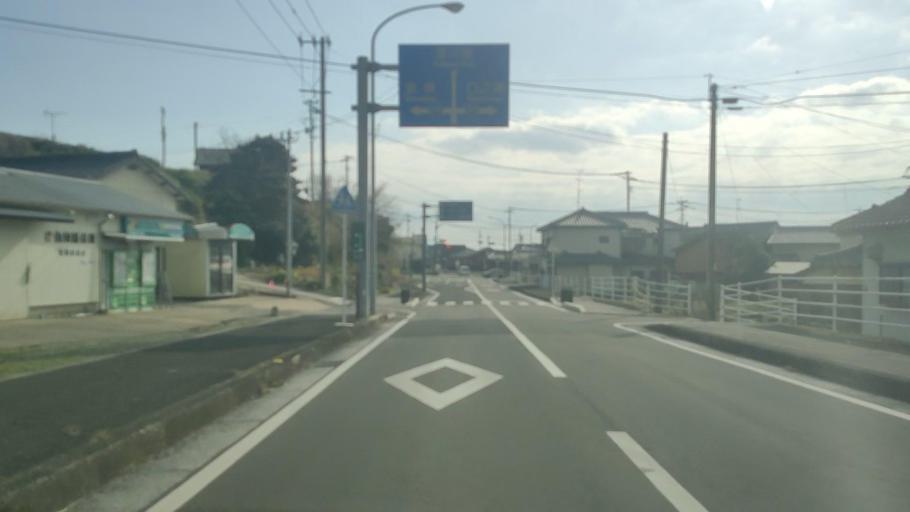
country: JP
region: Nagasaki
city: Shimabara
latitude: 32.6555
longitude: 130.2884
